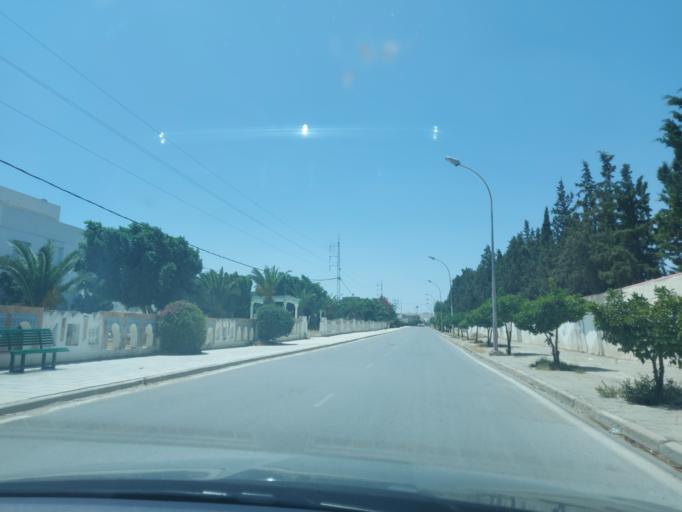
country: TN
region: Silyanah
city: Siliana
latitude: 36.0852
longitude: 9.3612
